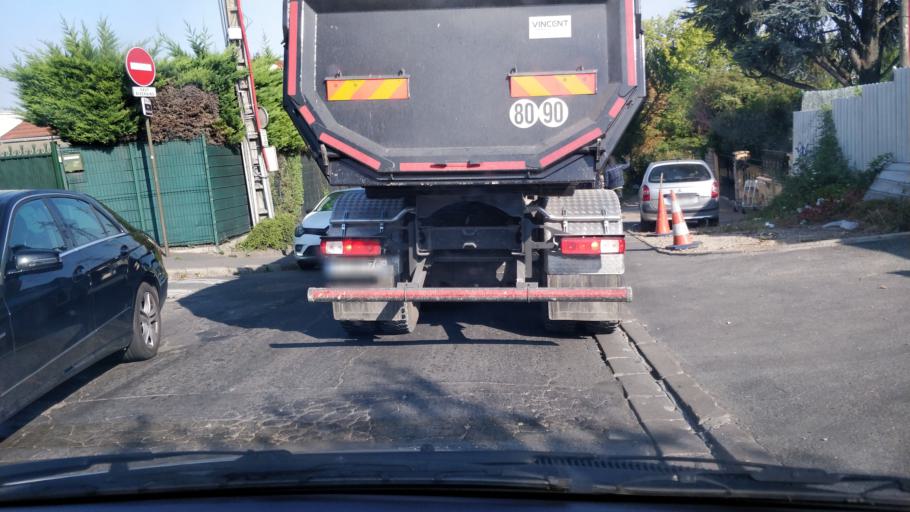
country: FR
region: Ile-de-France
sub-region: Departement de Seine-Saint-Denis
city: Villemomble
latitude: 48.8781
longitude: 2.4978
